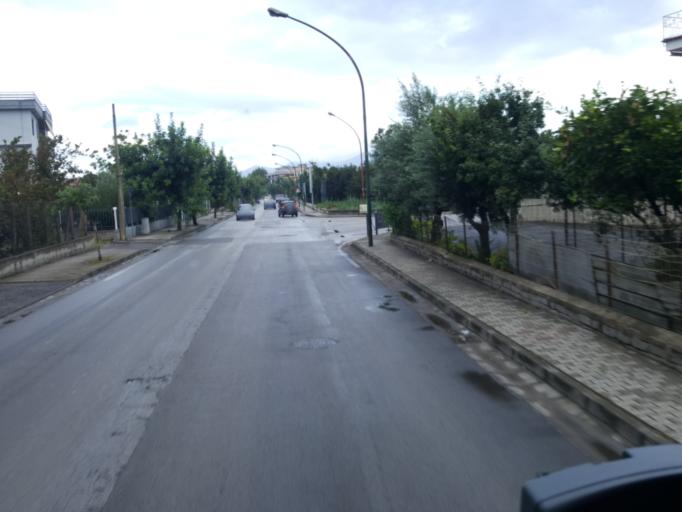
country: IT
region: Campania
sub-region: Provincia di Napoli
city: Palma Campania
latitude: 40.8639
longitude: 14.5485
